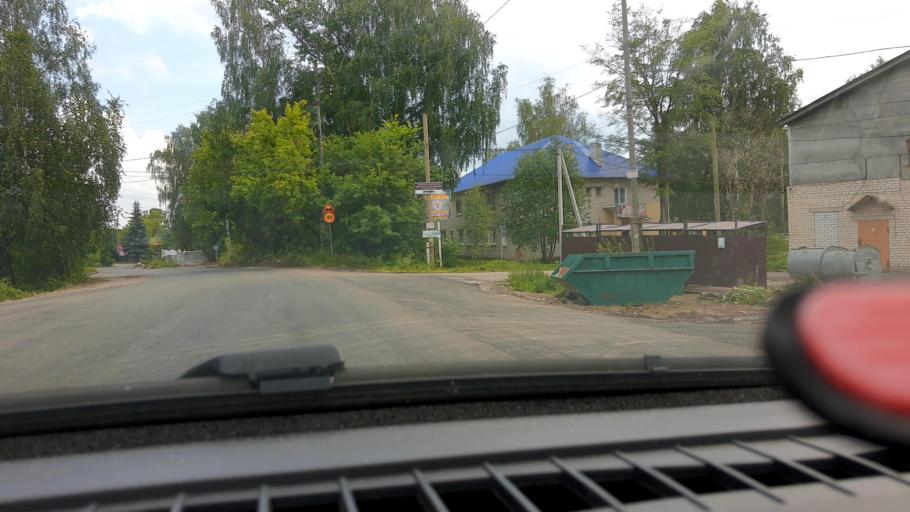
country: RU
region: Nizjnij Novgorod
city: Gorodets
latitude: 56.6312
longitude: 43.4770
